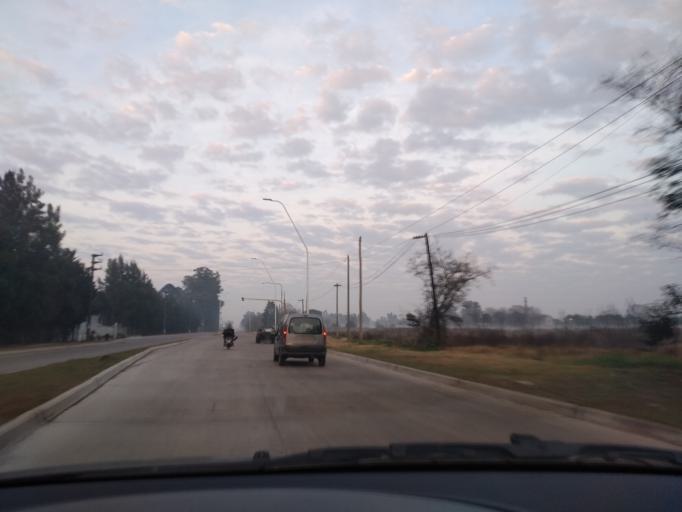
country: AR
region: Buenos Aires
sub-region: Partido de La Plata
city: La Plata
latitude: -34.9920
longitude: -58.0073
